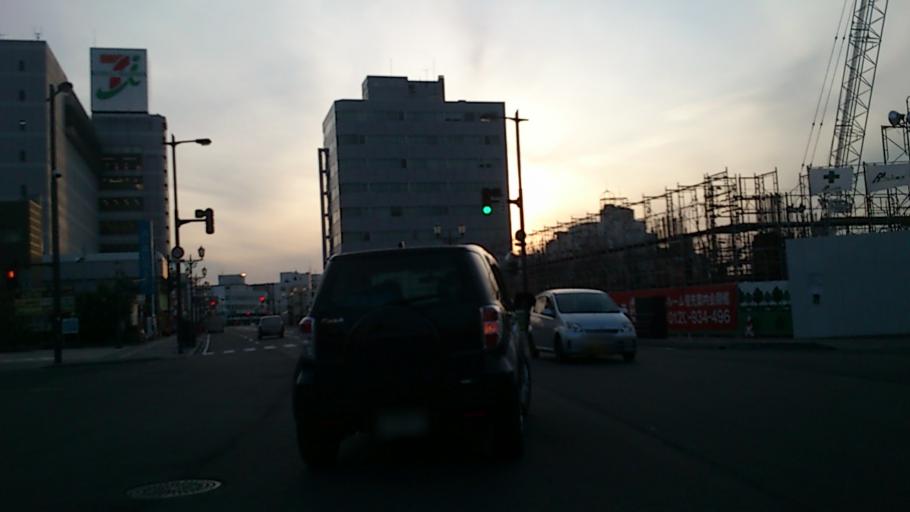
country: JP
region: Aomori
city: Hirosaki
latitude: 40.5998
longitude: 140.4830
